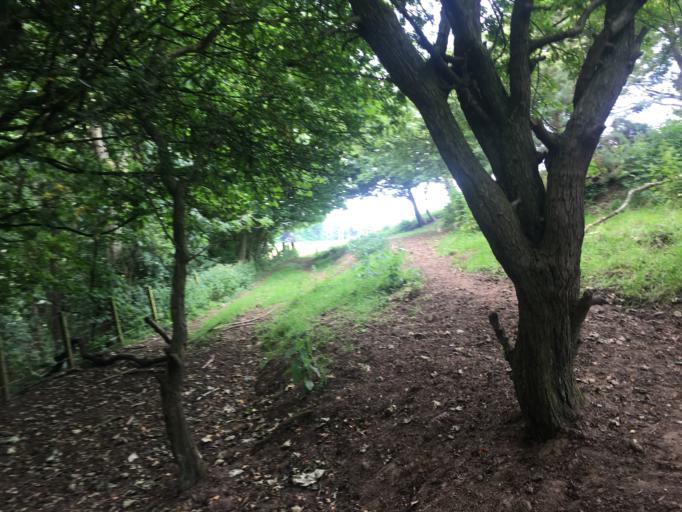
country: GB
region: England
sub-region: Northumberland
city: Belford
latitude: 55.6021
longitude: -1.7767
